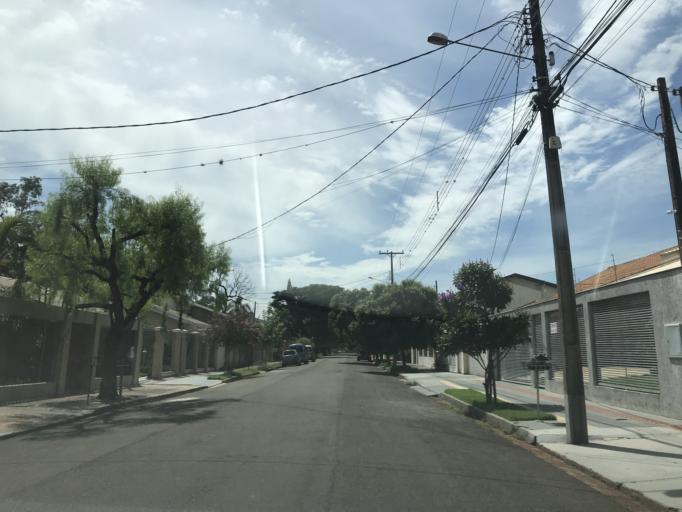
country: BR
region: Parana
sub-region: Londrina
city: Londrina
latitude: -23.3436
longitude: -51.1563
